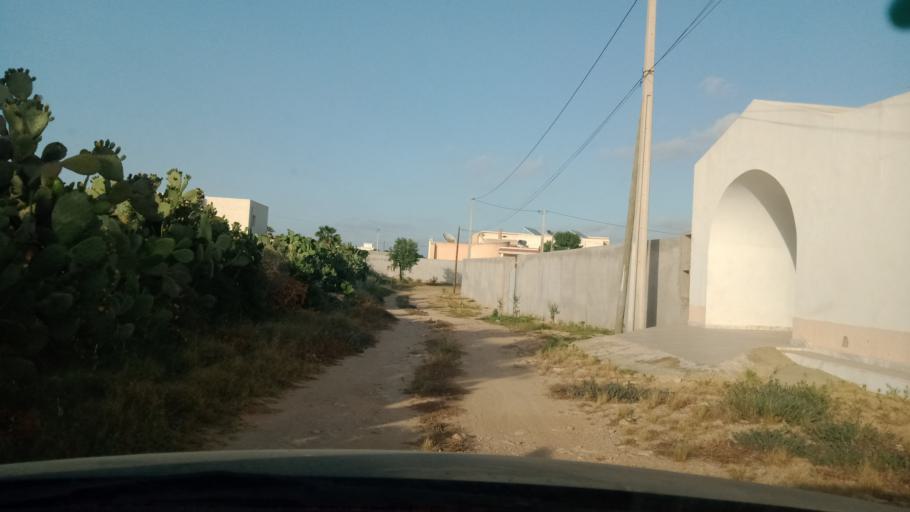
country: TN
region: Safaqis
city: Al Qarmadah
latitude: 34.8211
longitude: 10.7498
